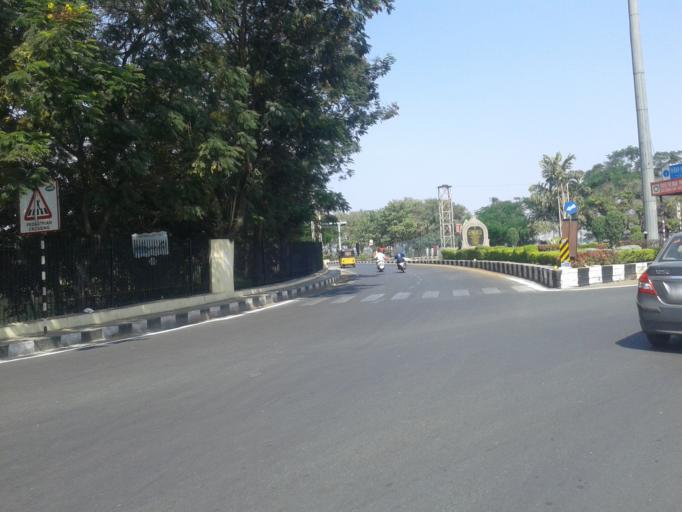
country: IN
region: Telangana
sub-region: Hyderabad
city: Hyderabad
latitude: 17.4150
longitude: 78.4657
